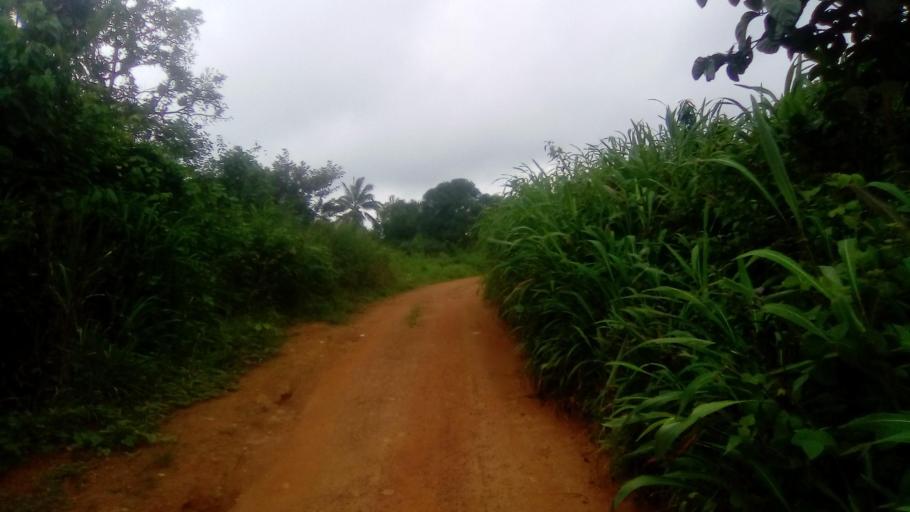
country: SL
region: Eastern Province
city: Kailahun
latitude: 8.3059
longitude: -10.5600
